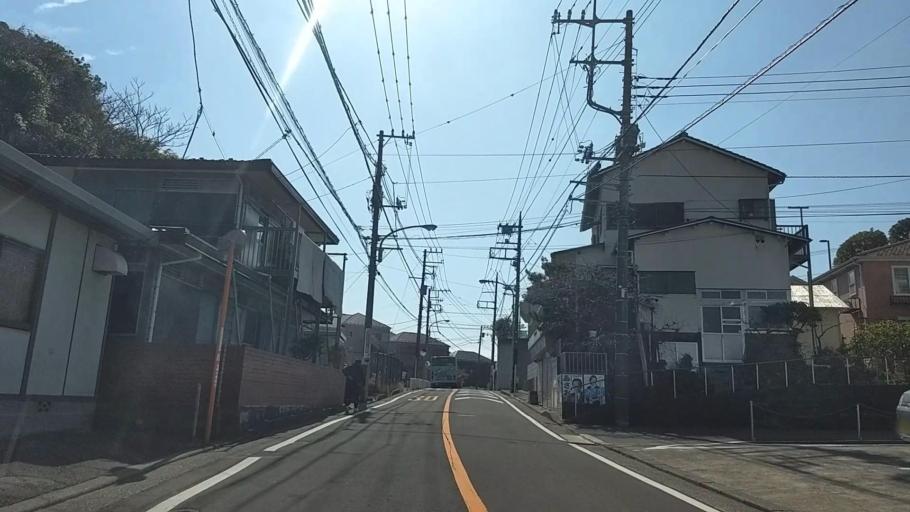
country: JP
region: Kanagawa
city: Kamakura
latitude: 35.3680
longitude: 139.5399
